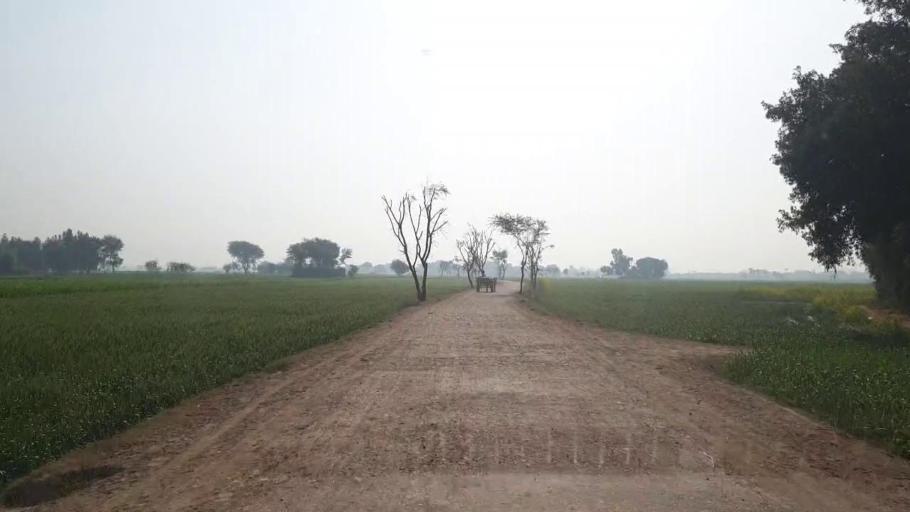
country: PK
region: Sindh
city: Bhit Shah
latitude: 25.7350
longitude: 68.5196
